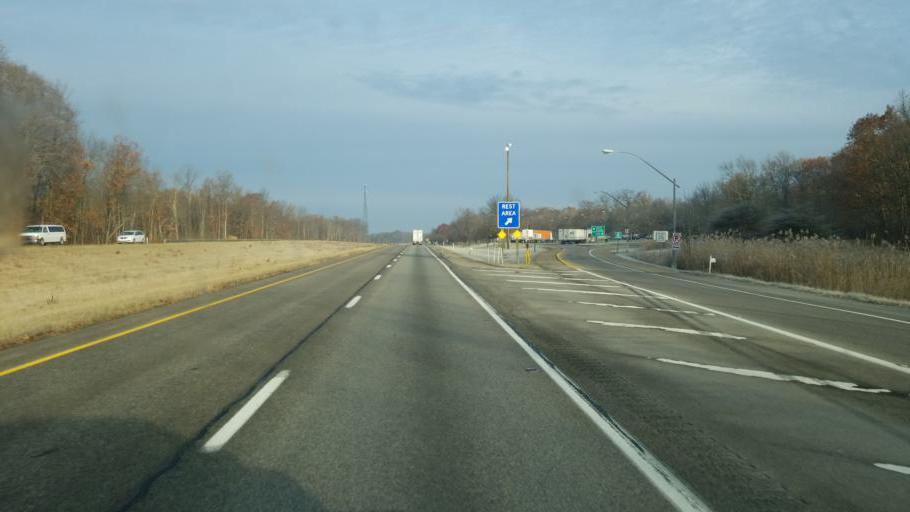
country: US
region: Pennsylvania
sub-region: Mercer County
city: Stoneboro
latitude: 41.4530
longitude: -80.1616
